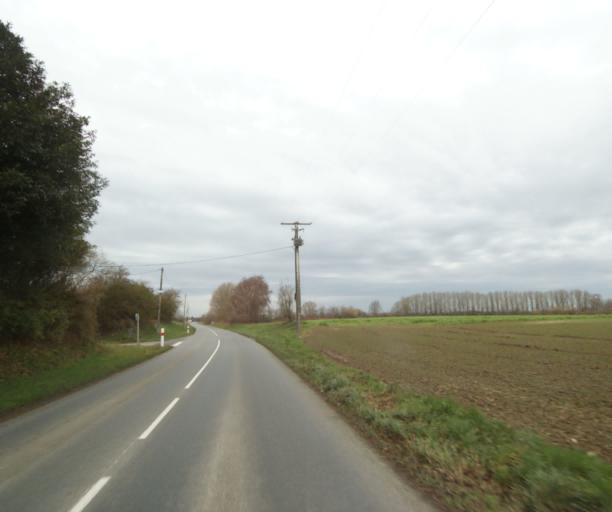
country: FR
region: Nord-Pas-de-Calais
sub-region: Departement du Nord
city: Saultain
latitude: 50.3586
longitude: 3.5915
